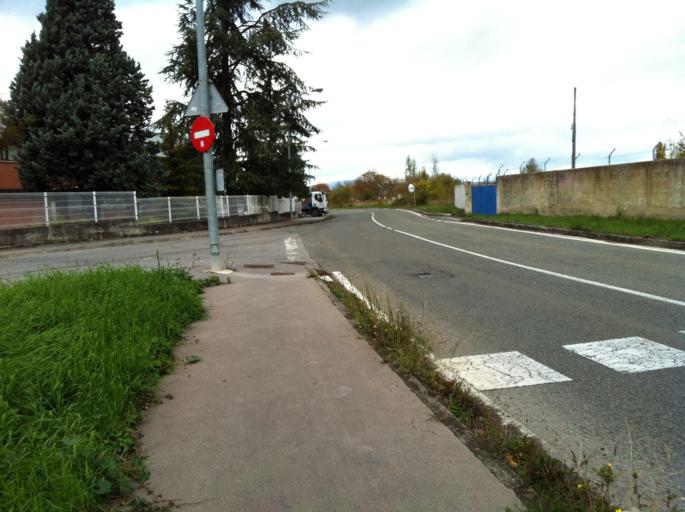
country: ES
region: Basque Country
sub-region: Provincia de Alava
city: Gasteiz / Vitoria
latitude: 42.8295
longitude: -2.6532
